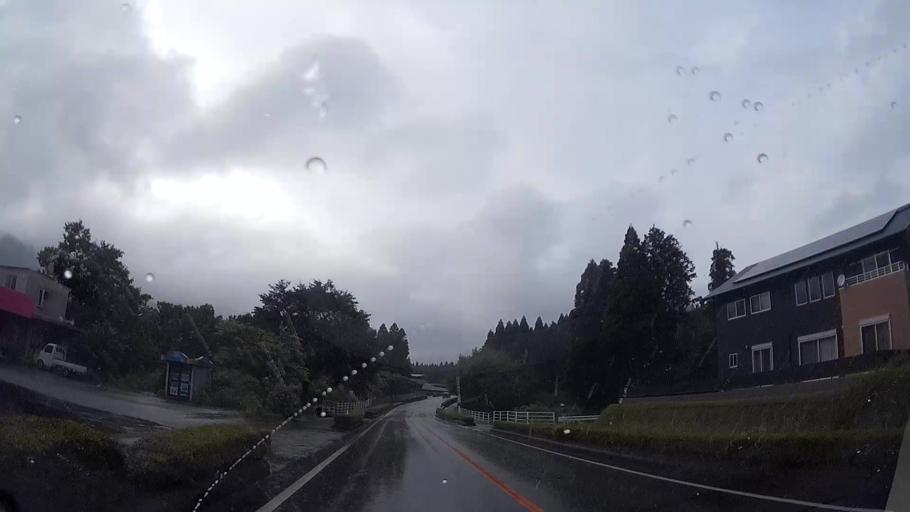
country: JP
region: Kumamoto
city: Aso
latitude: 32.8611
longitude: 131.0027
